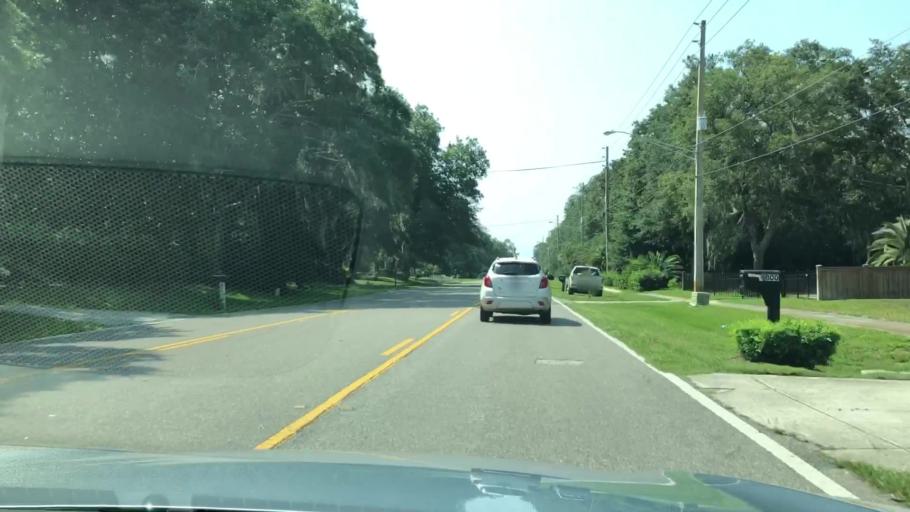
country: US
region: Florida
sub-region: Duval County
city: Neptune Beach
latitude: 30.3185
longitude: -81.4083
